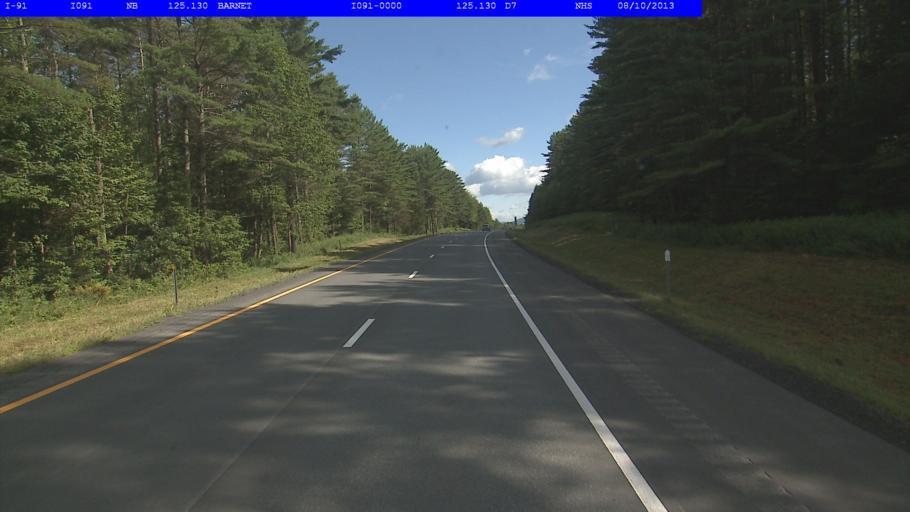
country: US
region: Vermont
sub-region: Caledonia County
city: Saint Johnsbury
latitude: 44.3539
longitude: -72.0342
